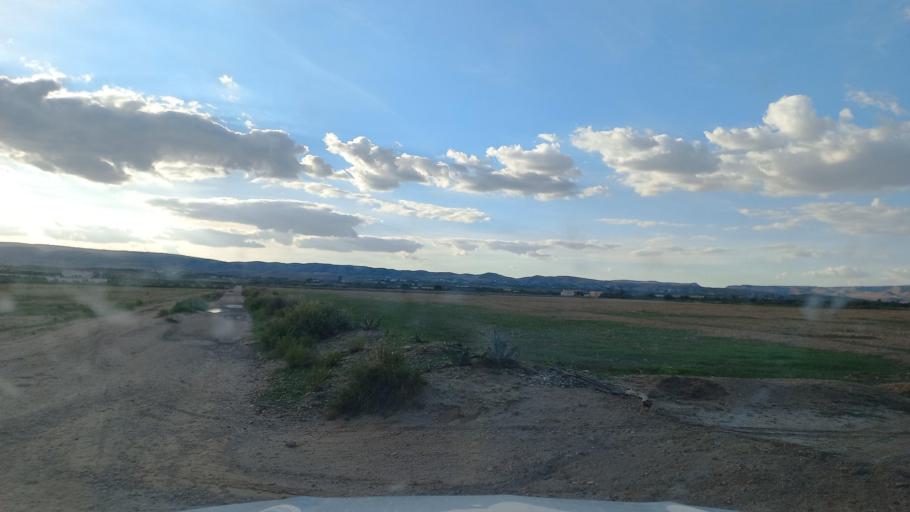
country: TN
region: Al Qasrayn
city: Sbiba
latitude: 35.3507
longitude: 9.0404
